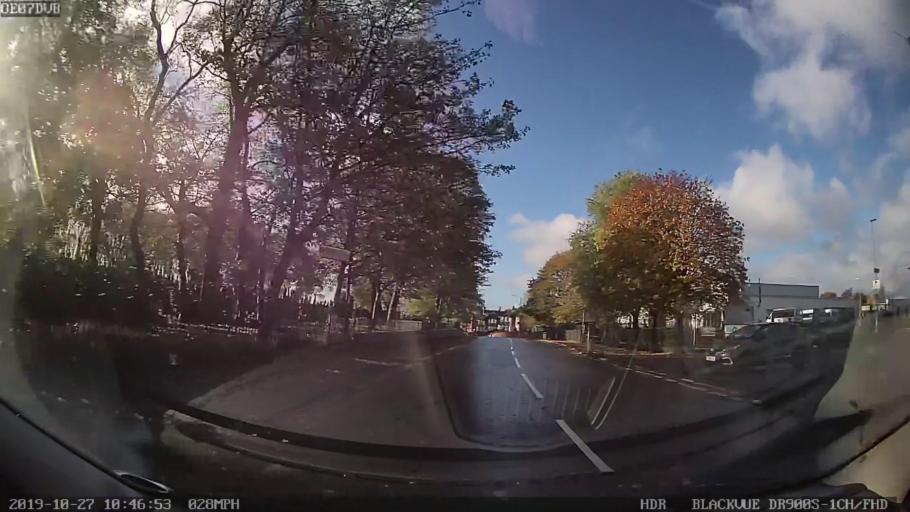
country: GB
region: England
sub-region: Manchester
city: Failsworth
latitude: 53.5172
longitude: -2.1881
